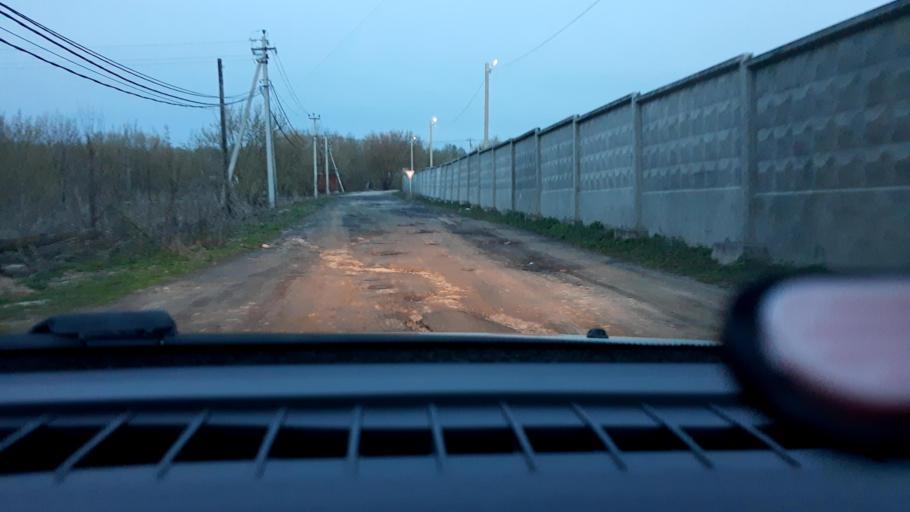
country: RU
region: Nizjnij Novgorod
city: Afonino
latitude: 56.1999
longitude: 44.0095
